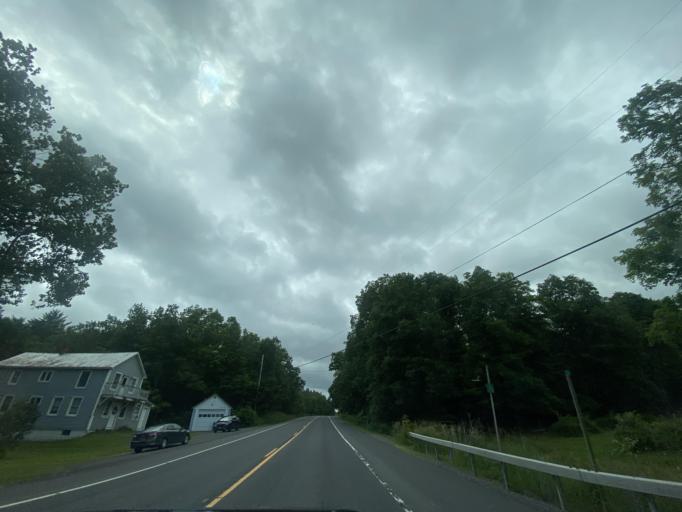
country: US
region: New York
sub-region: Greene County
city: Cairo
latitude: 42.3935
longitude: -73.9528
